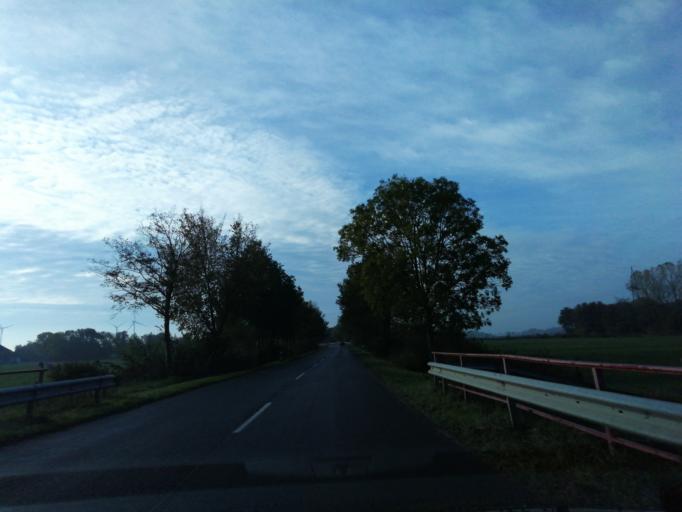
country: DE
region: Lower Saxony
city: Sillenstede
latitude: 53.6295
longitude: 8.0153
